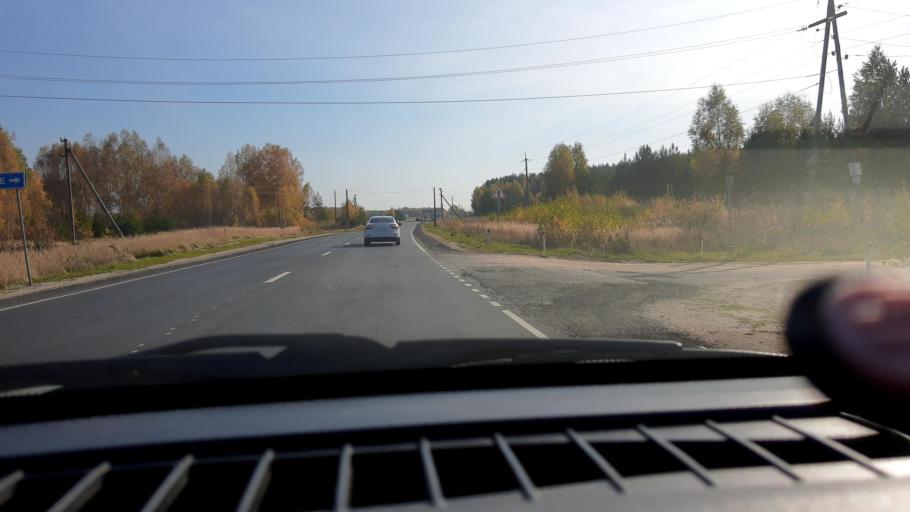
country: RU
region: Nizjnij Novgorod
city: Novaya Balakhna
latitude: 56.6118
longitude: 43.5992
